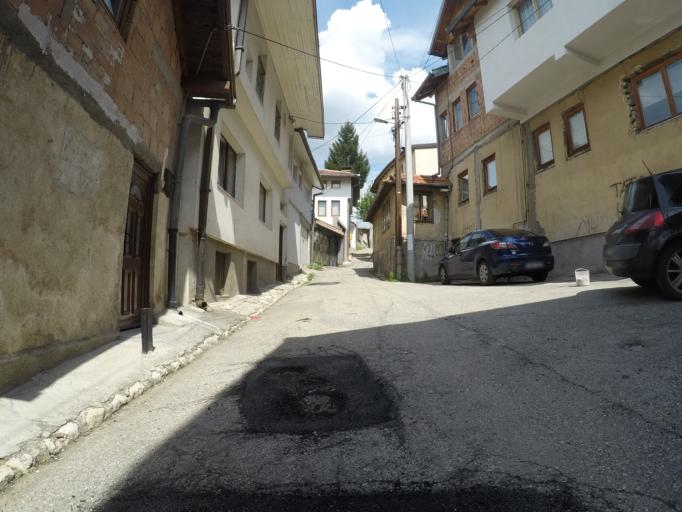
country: BA
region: Federation of Bosnia and Herzegovina
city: Kobilja Glava
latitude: 43.8562
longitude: 18.4375
